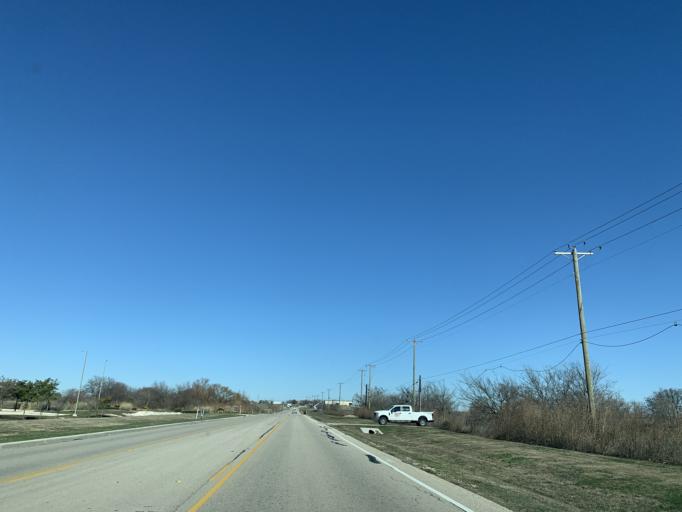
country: US
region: Texas
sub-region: Williamson County
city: Hutto
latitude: 30.5538
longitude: -97.5717
